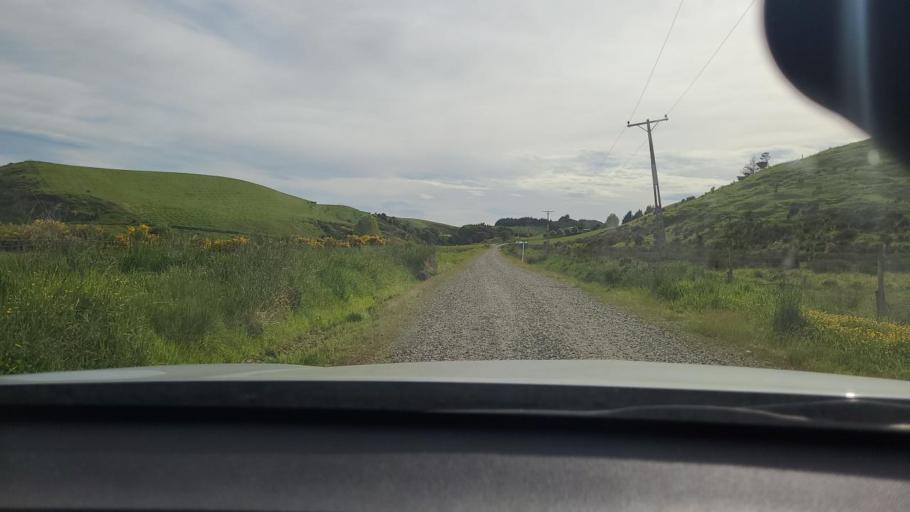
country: NZ
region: Southland
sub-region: Southland District
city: Riverton
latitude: -46.1179
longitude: 167.7211
